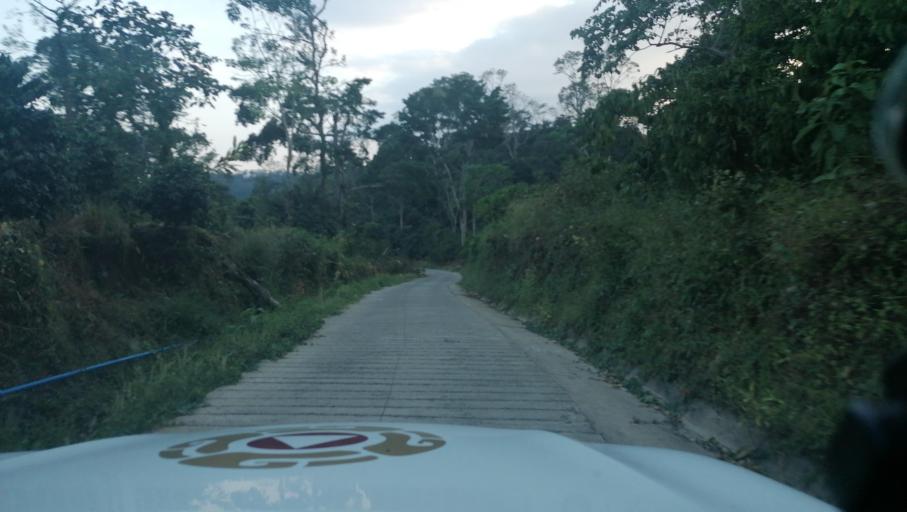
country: MX
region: Chiapas
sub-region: Cacahoatan
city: Benito Juarez
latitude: 15.0824
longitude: -92.2236
